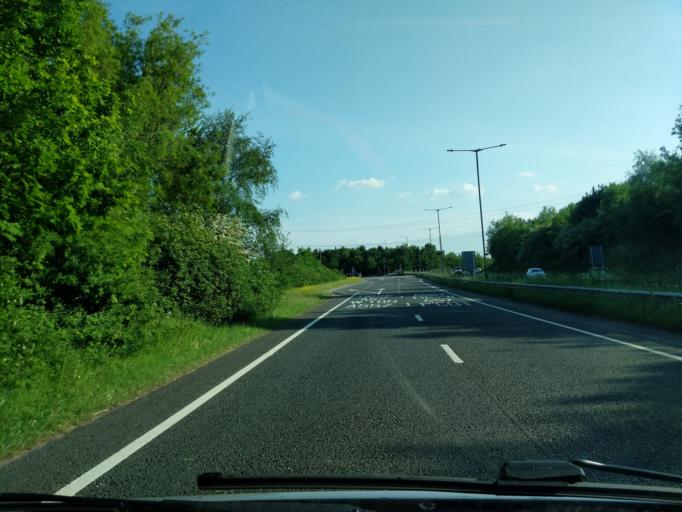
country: GB
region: England
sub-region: St. Helens
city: St Helens
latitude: 53.4062
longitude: -2.7444
